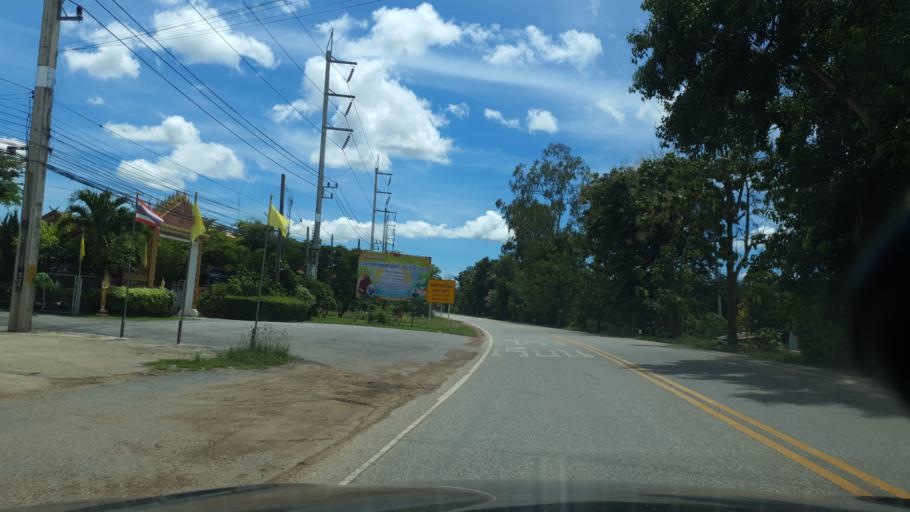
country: TH
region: Sukhothai
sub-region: Amphoe Si Satchanalai
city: Si Satchanalai
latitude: 17.5055
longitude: 99.7576
